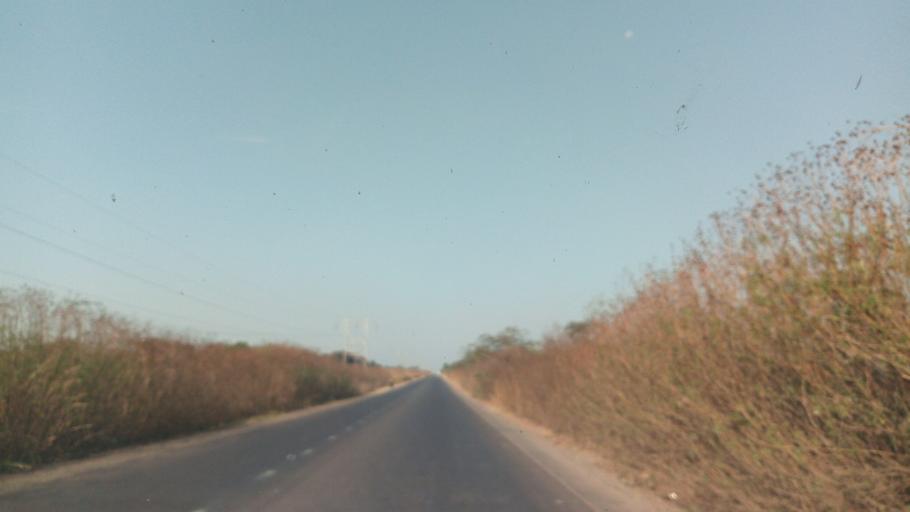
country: CD
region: Katanga
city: Likasi
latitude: -11.0024
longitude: 26.8559
